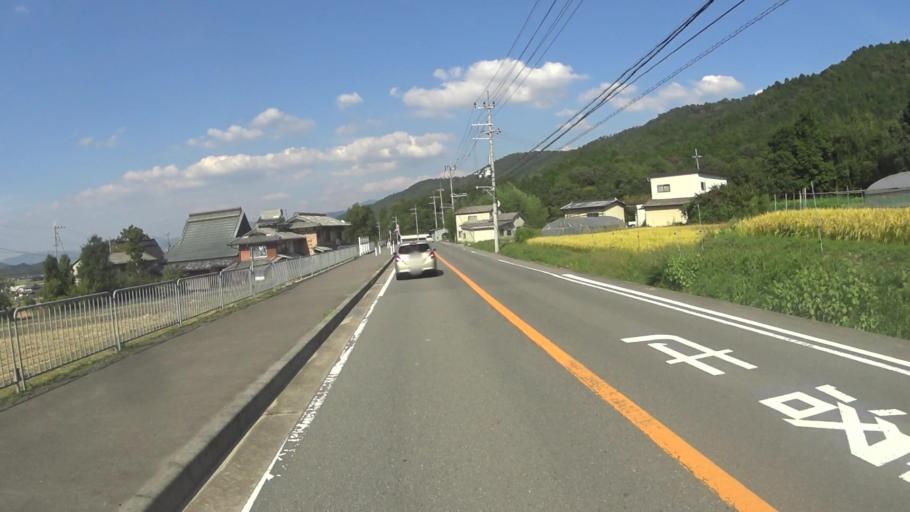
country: JP
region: Kyoto
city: Kameoka
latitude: 34.9801
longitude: 135.5449
